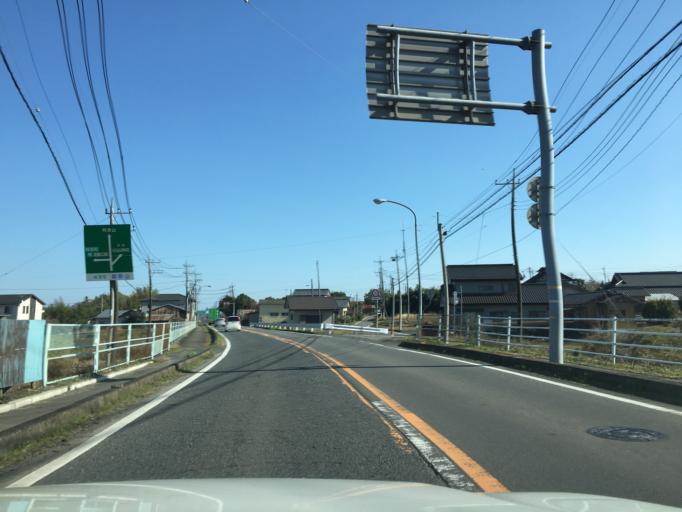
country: JP
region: Ibaraki
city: Omiya
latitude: 36.5408
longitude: 140.3376
